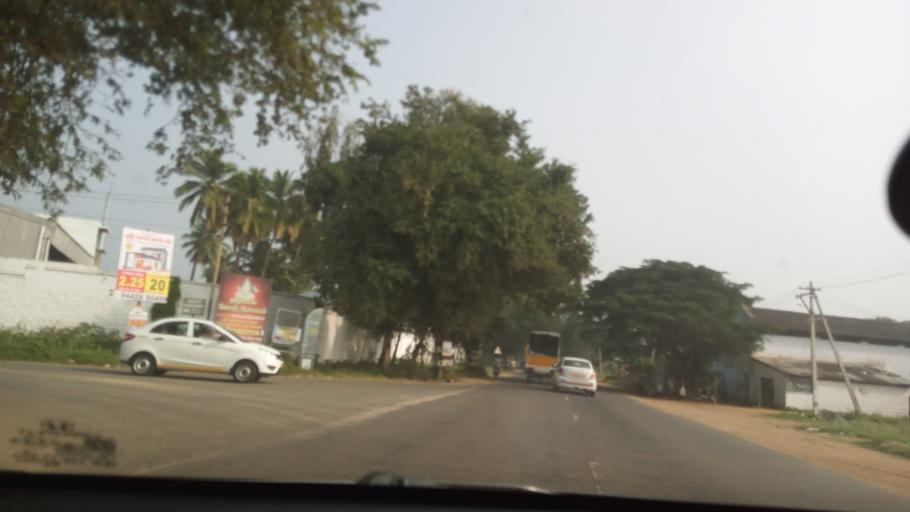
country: IN
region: Tamil Nadu
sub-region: Coimbatore
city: Annur
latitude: 11.1799
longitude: 77.0602
